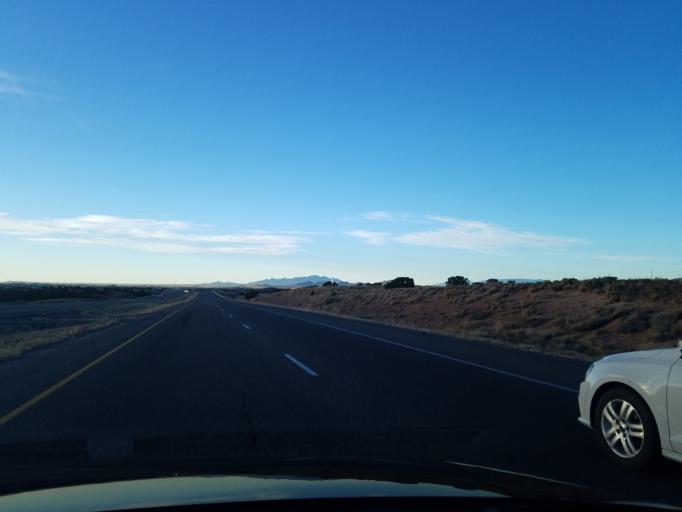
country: US
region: New Mexico
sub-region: Santa Fe County
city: Agua Fria
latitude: 35.6266
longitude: -106.0709
